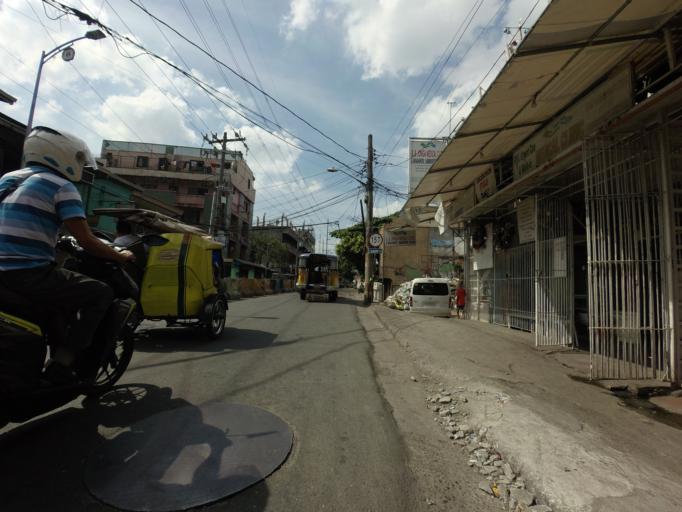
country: PH
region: Metro Manila
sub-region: City of Manila
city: Quiapo
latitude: 14.5725
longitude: 120.9990
